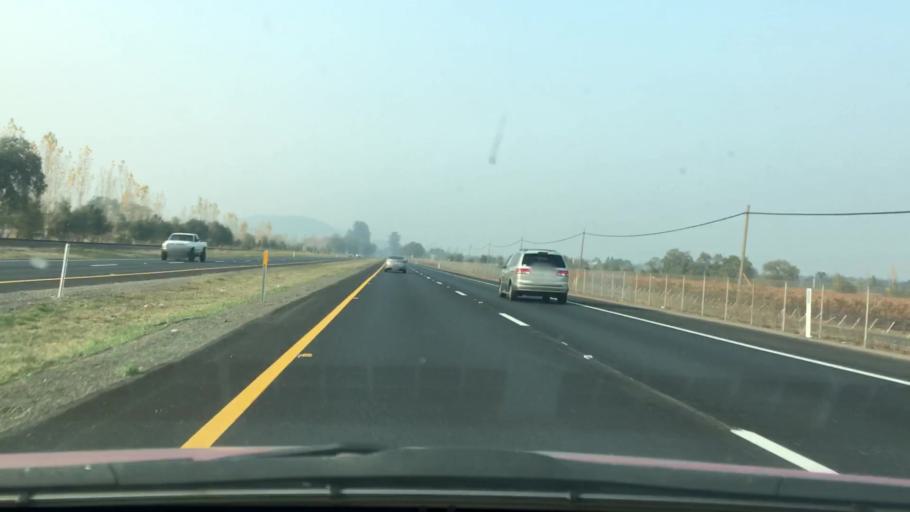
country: US
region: California
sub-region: Napa County
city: Yountville
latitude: 38.3793
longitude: -122.3452
